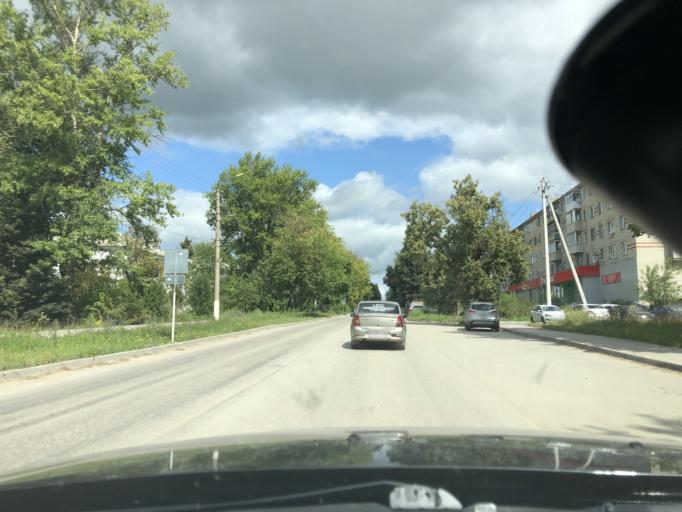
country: RU
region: Tula
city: Yasnogorsk
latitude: 54.4691
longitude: 37.7004
